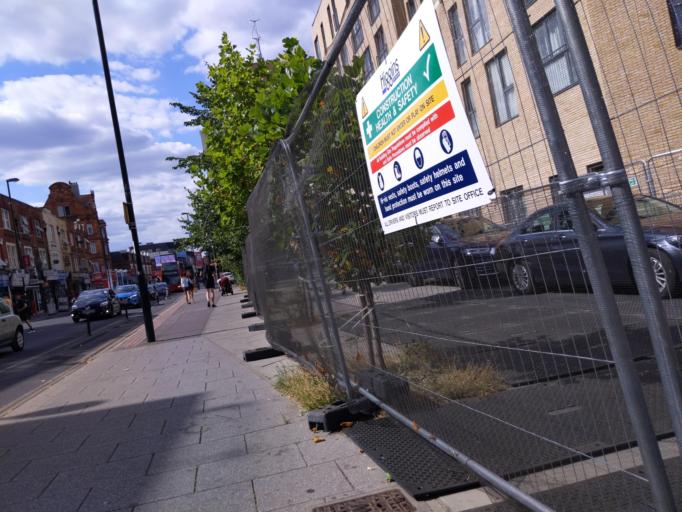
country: GB
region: England
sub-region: Greater London
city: Croydon
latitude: 51.3847
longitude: -0.1090
